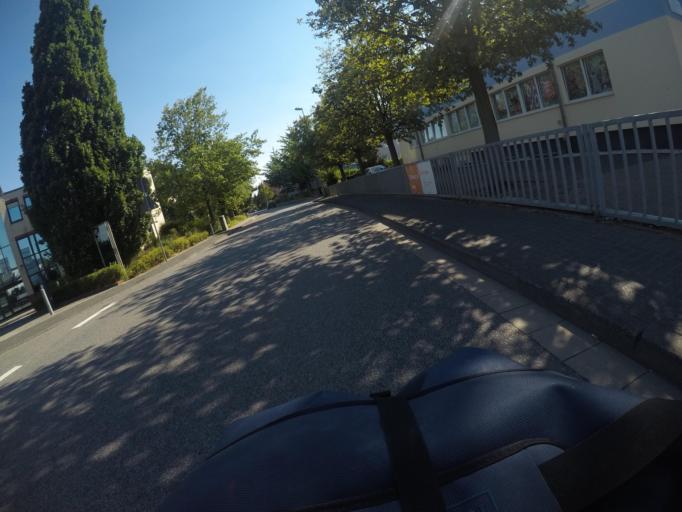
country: DE
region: Hesse
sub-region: Regierungsbezirk Darmstadt
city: Hochheim am Main
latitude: 50.0586
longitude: 8.3348
